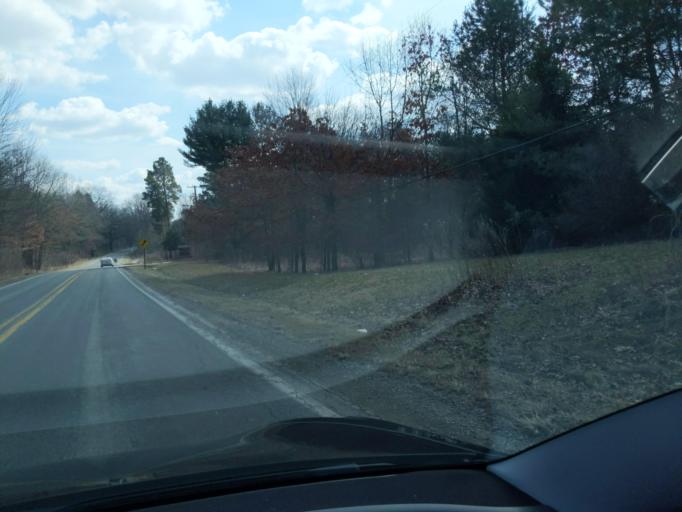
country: US
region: Michigan
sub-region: Livingston County
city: Pinckney
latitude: 42.3914
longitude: -83.9345
